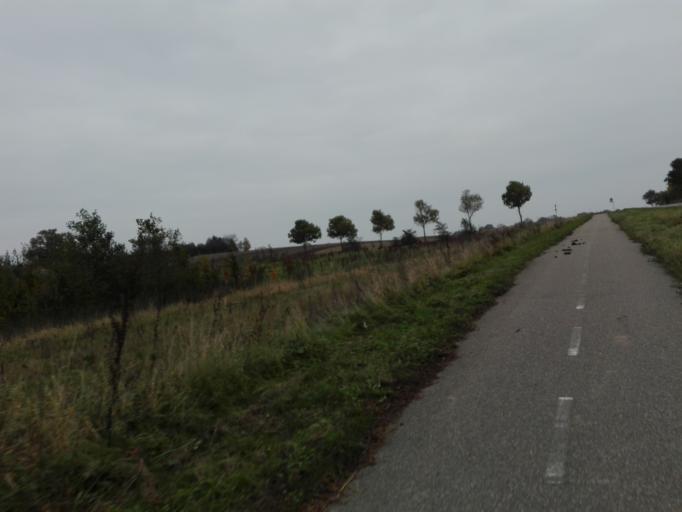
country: DK
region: Central Jutland
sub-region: Arhus Kommune
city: Beder
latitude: 56.0401
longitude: 10.2259
